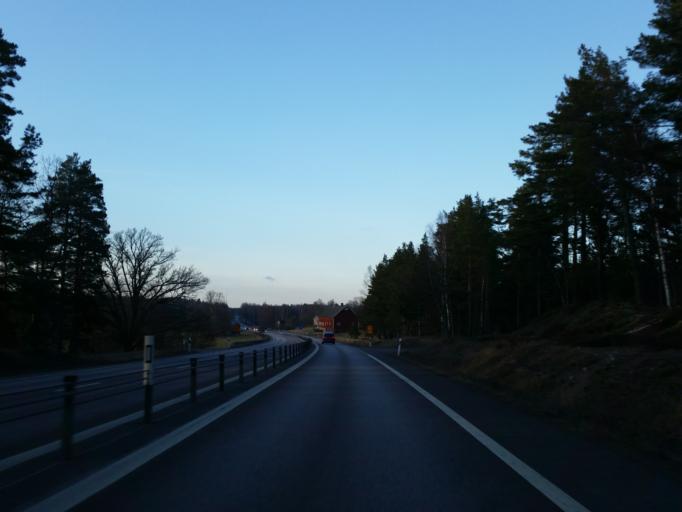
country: SE
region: Kalmar
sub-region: Oskarshamns Kommun
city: Oskarshamn
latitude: 57.4058
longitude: 16.4819
